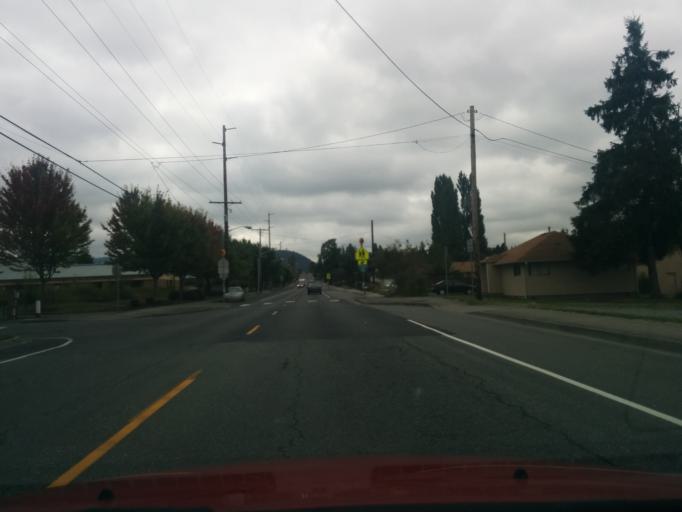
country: US
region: Washington
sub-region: Skagit County
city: Mount Vernon
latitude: 48.4324
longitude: -122.3135
